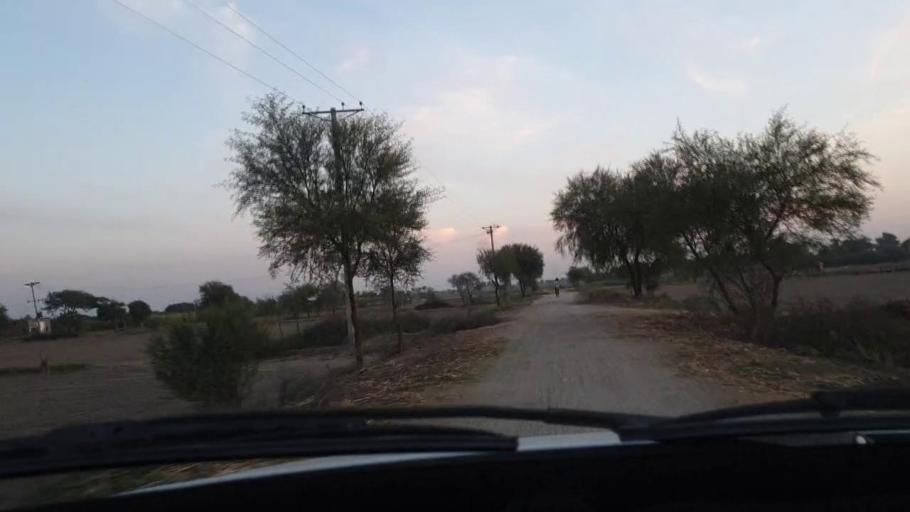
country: PK
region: Sindh
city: Tando Muhammad Khan
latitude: 25.0817
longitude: 68.3984
